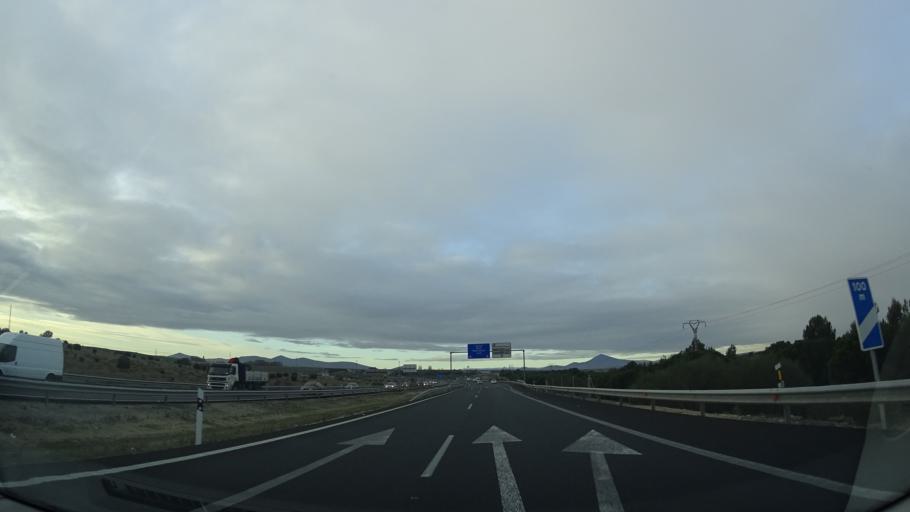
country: ES
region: Castille-La Mancha
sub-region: Province of Toledo
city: Burguillos de Toledo
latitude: 39.8271
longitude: -3.9813
